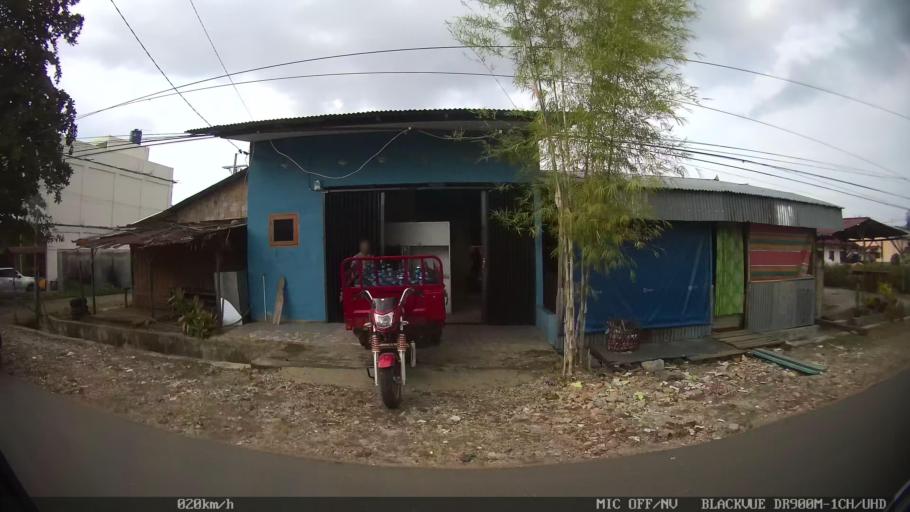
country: ID
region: North Sumatra
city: Sunggal
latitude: 3.5263
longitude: 98.6117
